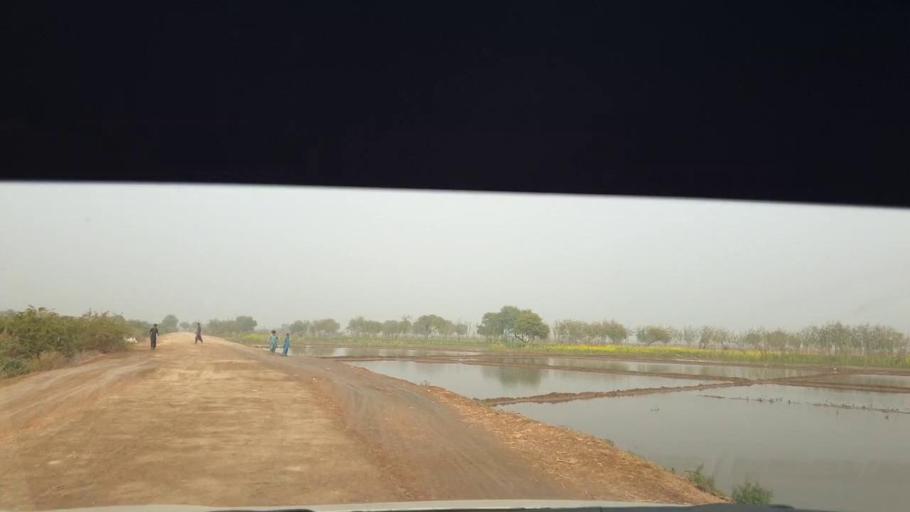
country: PK
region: Sindh
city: Berani
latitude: 25.8186
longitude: 68.8880
